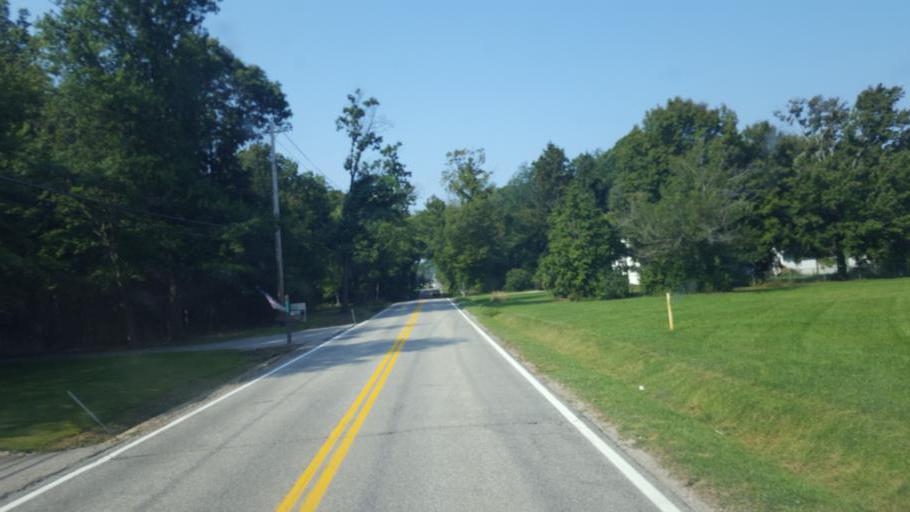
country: US
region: Ohio
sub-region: Lake County
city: Painesville
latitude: 41.6564
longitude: -81.2128
